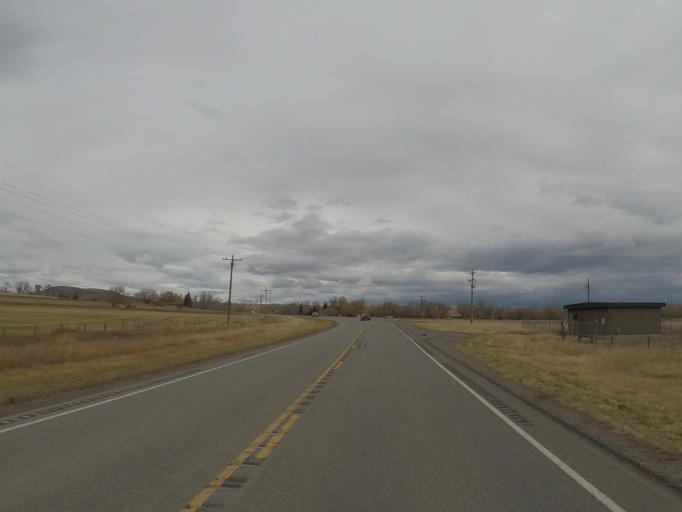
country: US
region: Montana
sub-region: Sweet Grass County
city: Big Timber
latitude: 45.8508
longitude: -109.9401
